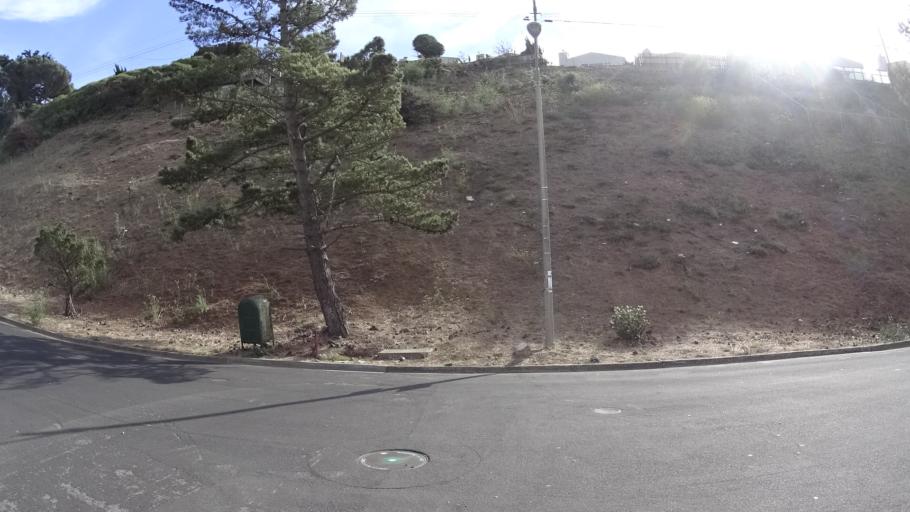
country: US
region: California
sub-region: San Mateo County
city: Daly City
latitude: 37.7069
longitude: -122.4294
